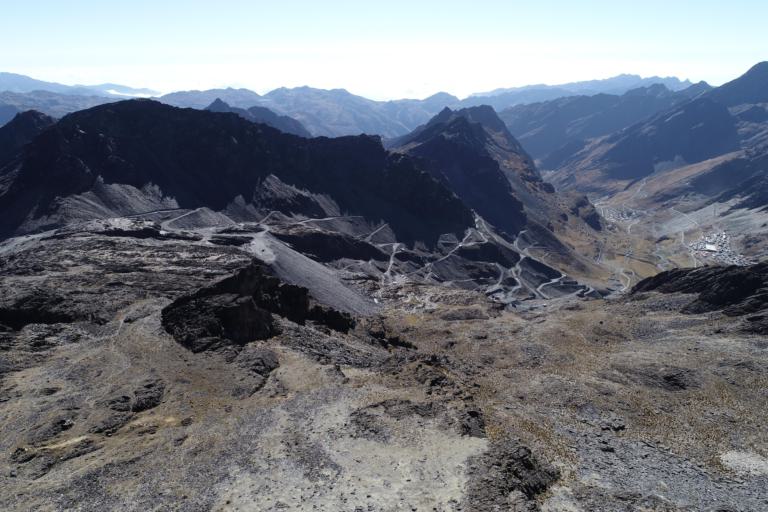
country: BO
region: La Paz
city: Sorata
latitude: -15.6745
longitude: -68.5677
